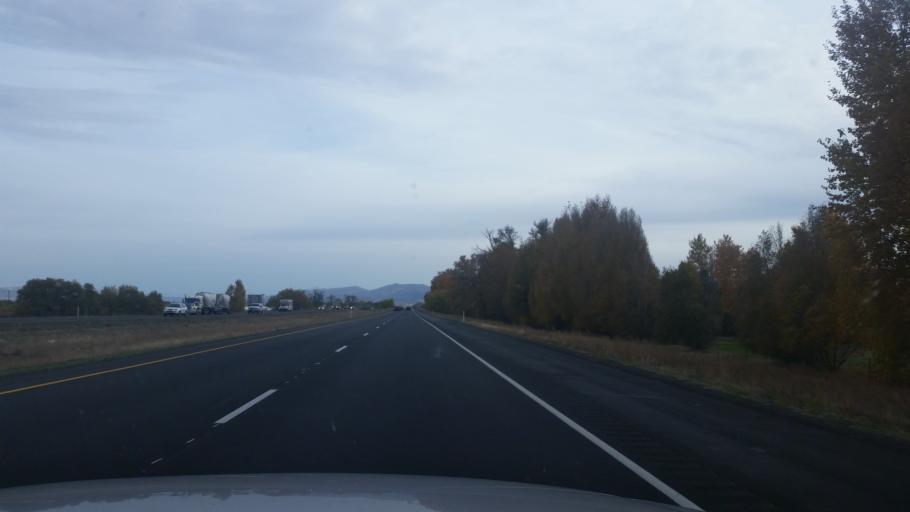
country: US
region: Washington
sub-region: Kittitas County
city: Ellensburg
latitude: 46.9933
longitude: -120.5757
